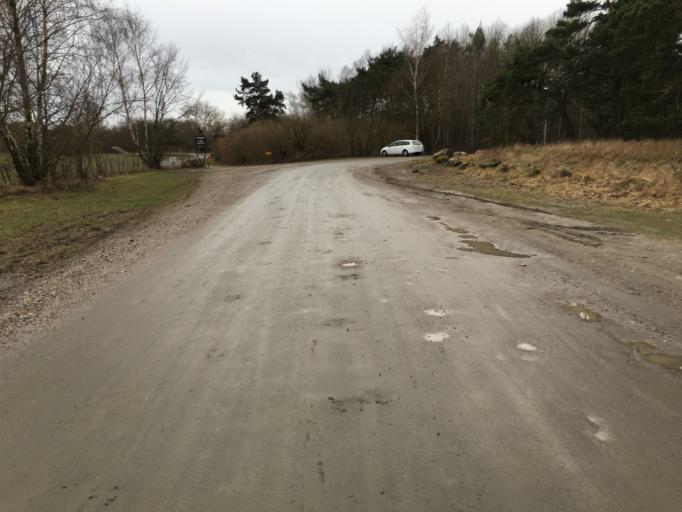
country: SE
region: Skane
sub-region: Lomma Kommun
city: Lomma
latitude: 55.6881
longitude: 13.0677
